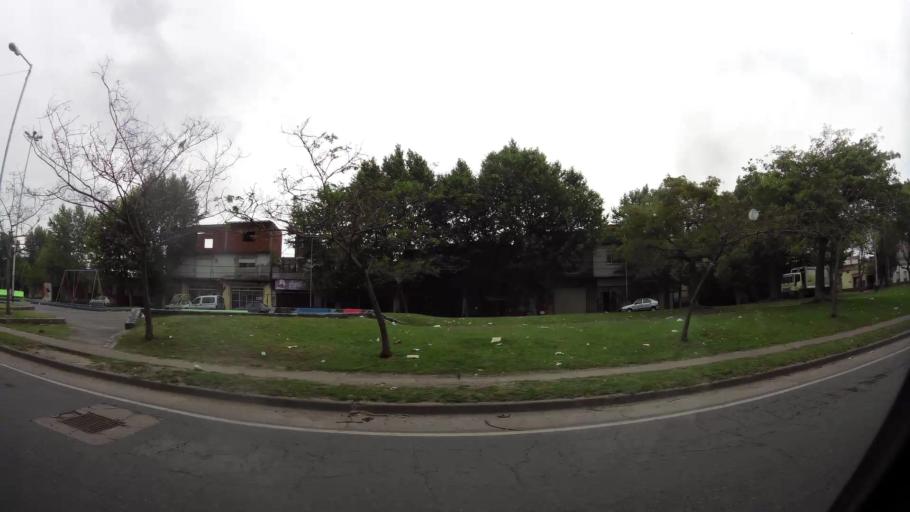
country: AR
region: Buenos Aires
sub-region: Partido de Avellaneda
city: Avellaneda
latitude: -34.6567
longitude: -58.3603
